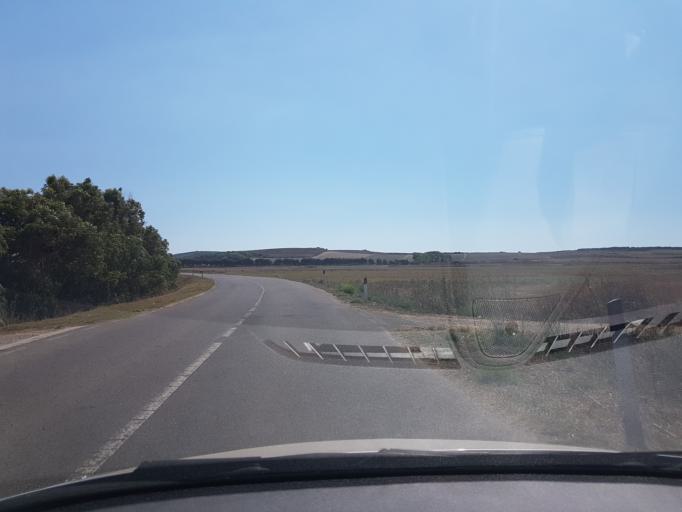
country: IT
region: Sardinia
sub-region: Provincia di Oristano
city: Nurachi
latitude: 39.9744
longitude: 8.4526
